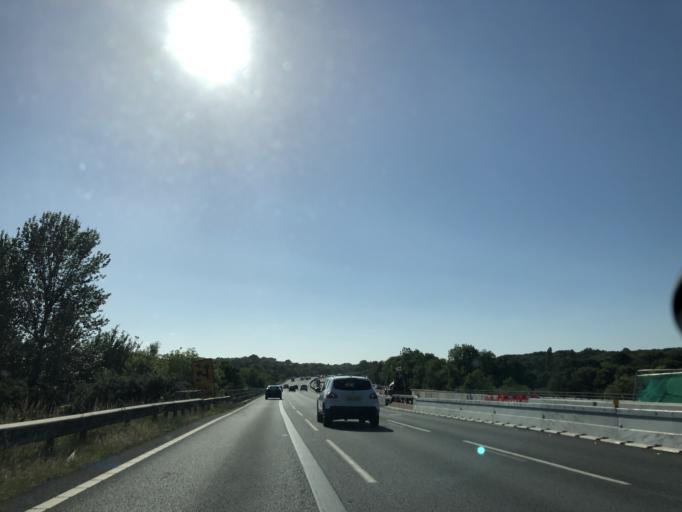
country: GB
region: England
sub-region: Hampshire
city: Fareham
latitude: 50.8671
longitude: -1.2231
